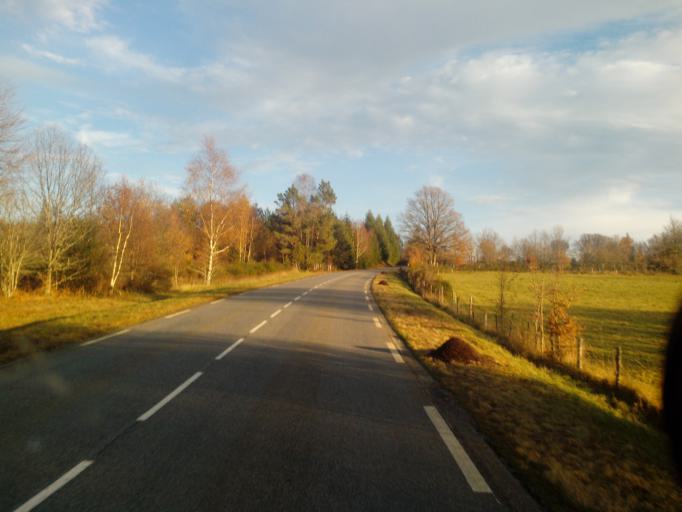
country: FR
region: Limousin
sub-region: Departement de la Correze
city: Bugeat
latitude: 45.5809
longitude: 2.0060
